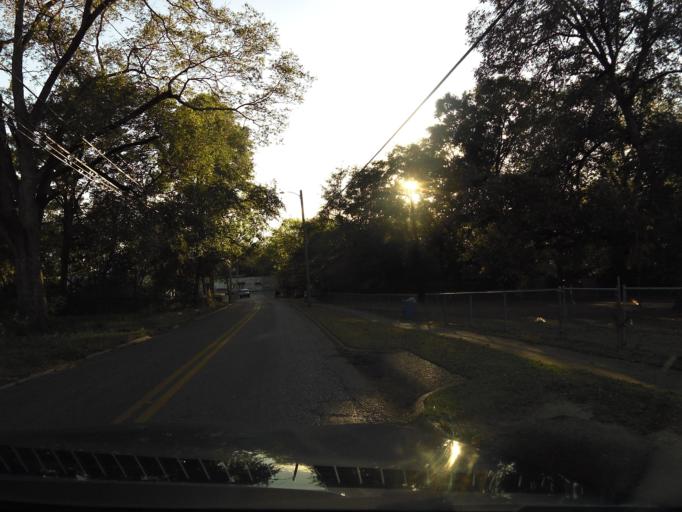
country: US
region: Alabama
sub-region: Houston County
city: Dothan
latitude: 31.2322
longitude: -85.3868
